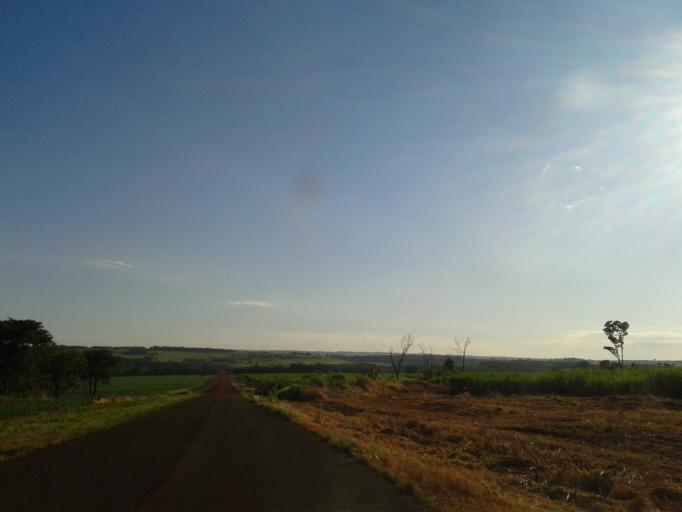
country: BR
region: Minas Gerais
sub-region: Centralina
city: Centralina
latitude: -18.7058
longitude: -49.2893
